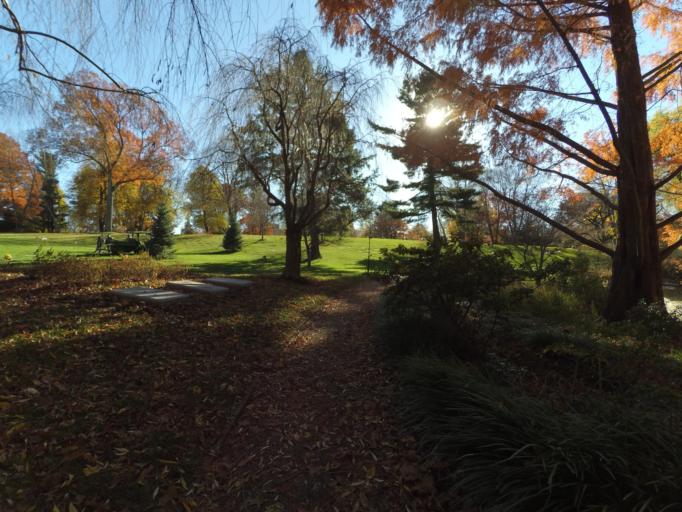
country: US
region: Massachusetts
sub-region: Middlesex County
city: Watertown
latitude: 42.3685
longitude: -71.1466
